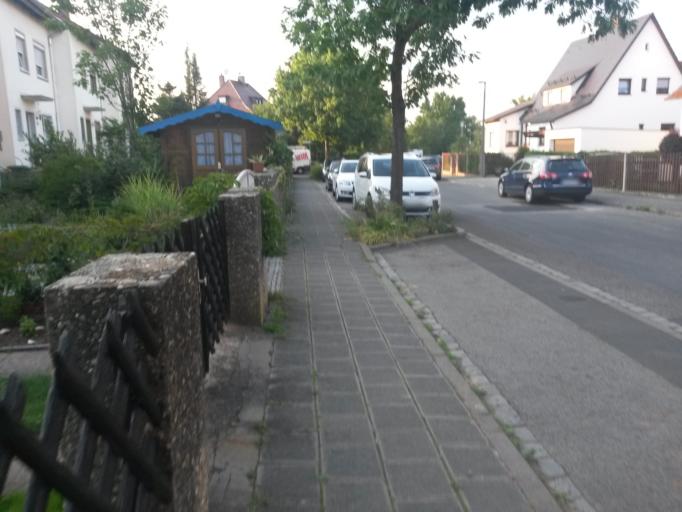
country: DE
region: Bavaria
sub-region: Regierungsbezirk Mittelfranken
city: Oberasbach
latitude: 49.4315
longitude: 10.9645
